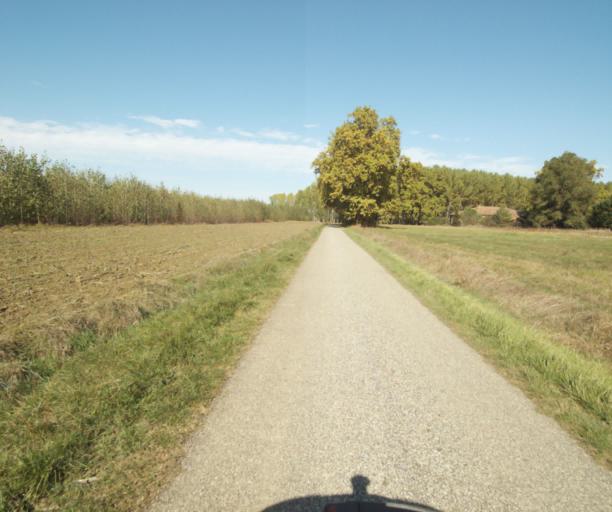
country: FR
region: Midi-Pyrenees
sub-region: Departement du Tarn-et-Garonne
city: Finhan
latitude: 43.9000
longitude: 1.2178
